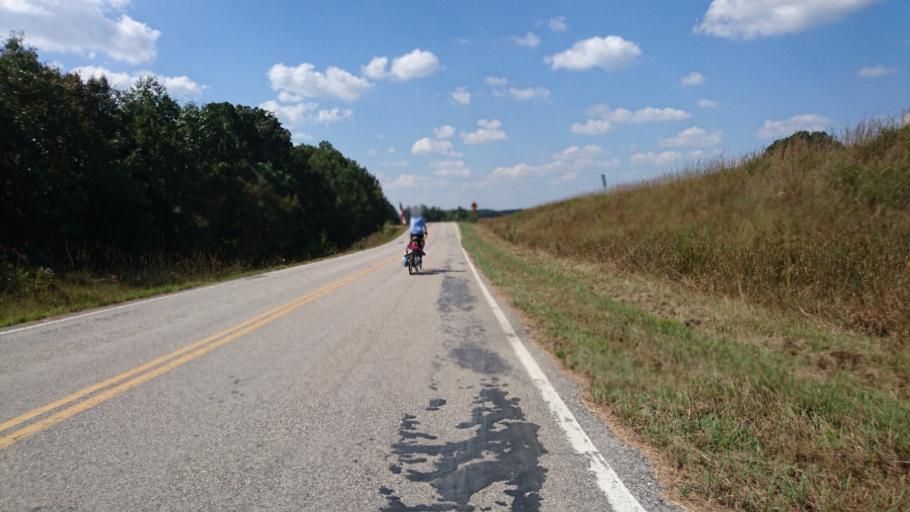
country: US
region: Missouri
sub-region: Pulaski County
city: Richland
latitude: 37.7542
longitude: -92.4856
